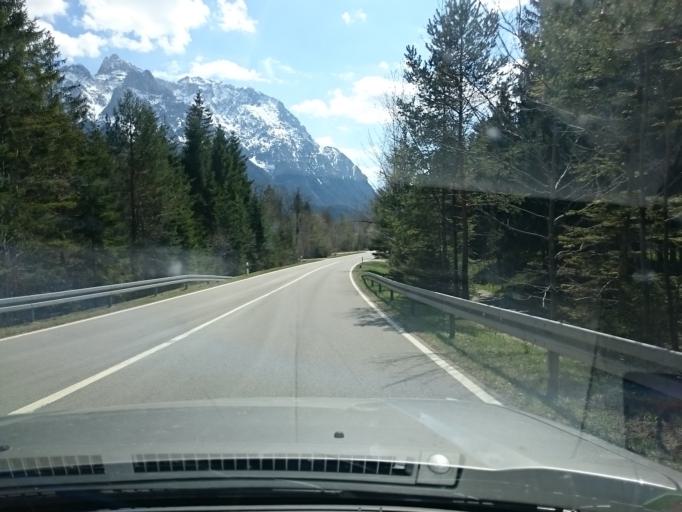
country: DE
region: Bavaria
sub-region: Upper Bavaria
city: Krun
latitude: 47.4689
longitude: 11.2804
